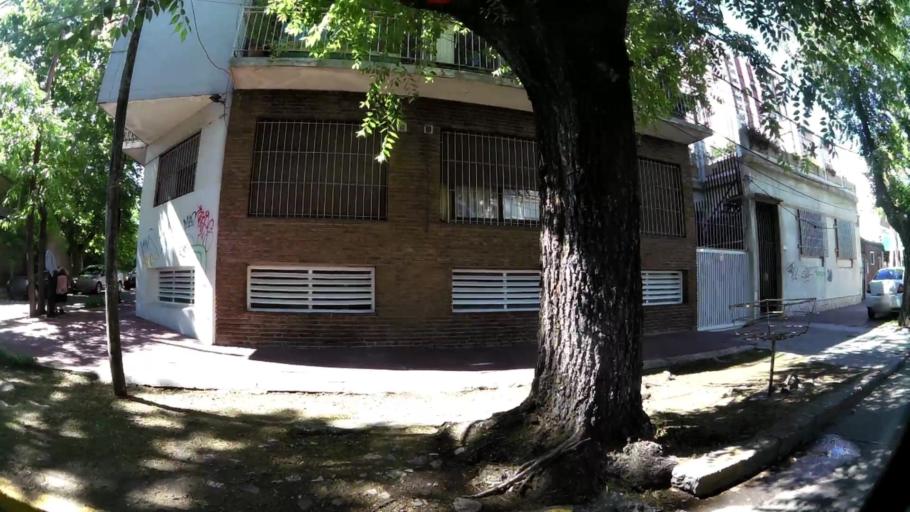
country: AR
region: Buenos Aires
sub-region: Partido de Vicente Lopez
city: Olivos
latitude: -34.5207
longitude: -58.4847
